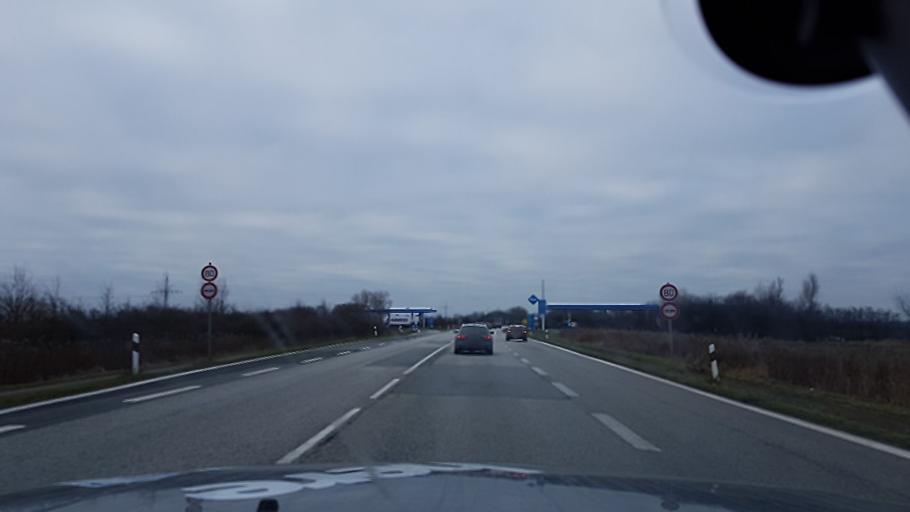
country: DE
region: Schleswig-Holstein
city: Grossenbrode
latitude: 54.3835
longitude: 11.0962
